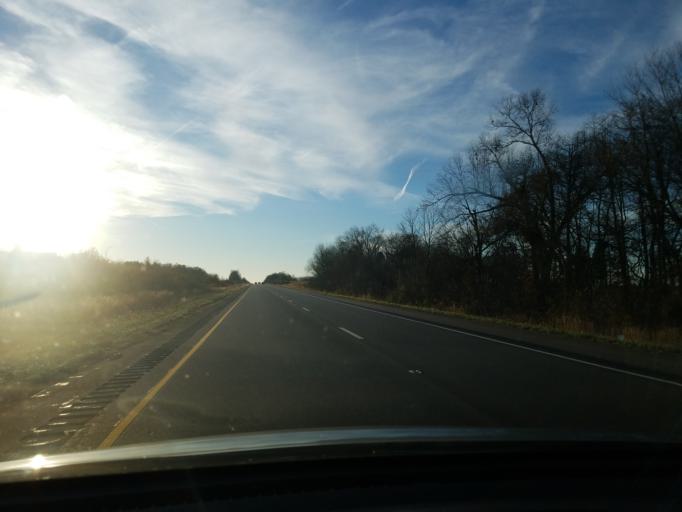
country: US
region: Indiana
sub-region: Spencer County
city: Dale
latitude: 38.2003
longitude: -87.1162
